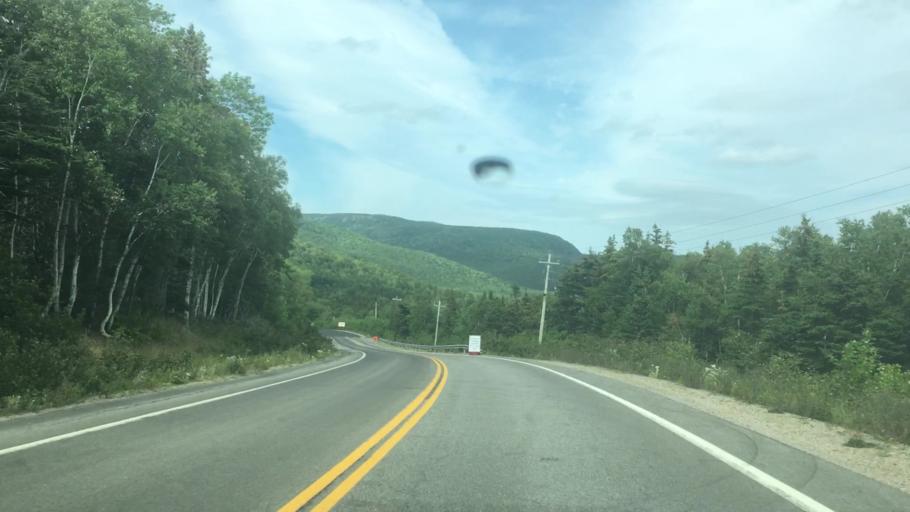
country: CA
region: Nova Scotia
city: Sydney Mines
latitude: 46.5409
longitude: -60.4139
